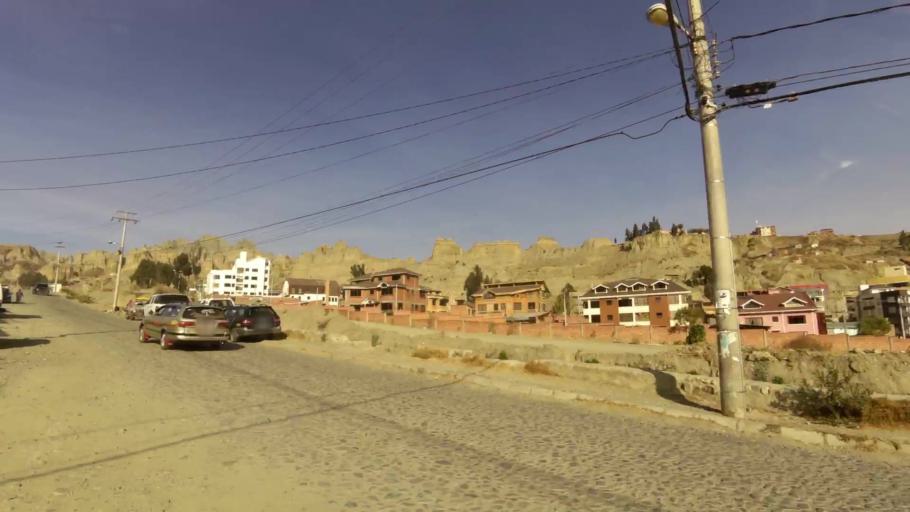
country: BO
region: La Paz
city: La Paz
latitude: -16.5034
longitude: -68.0819
